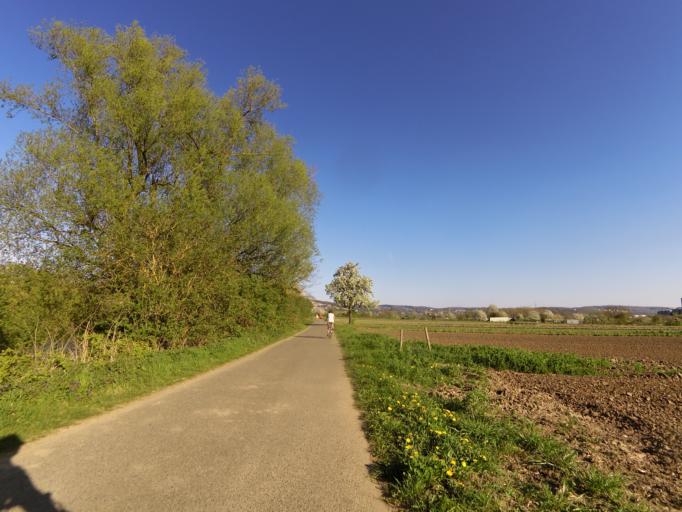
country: DE
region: Rheinland-Pfalz
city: Weitersburg
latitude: 50.4016
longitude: 7.5943
